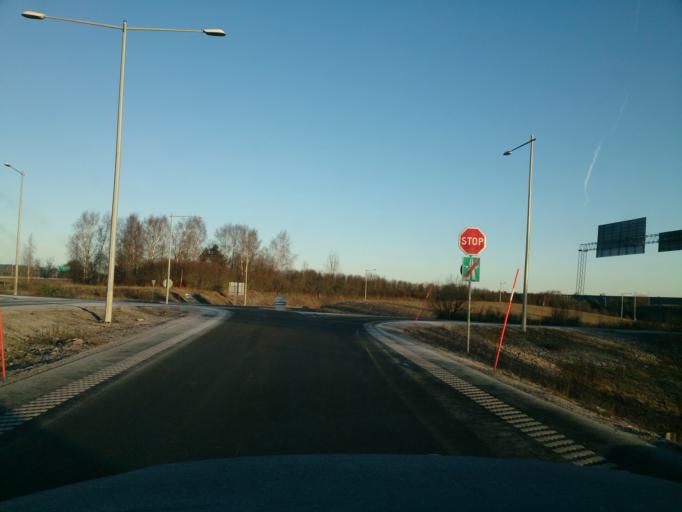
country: SE
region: OEstergoetland
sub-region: Norrkopings Kommun
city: Norrkoping
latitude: 58.6266
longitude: 16.1544
